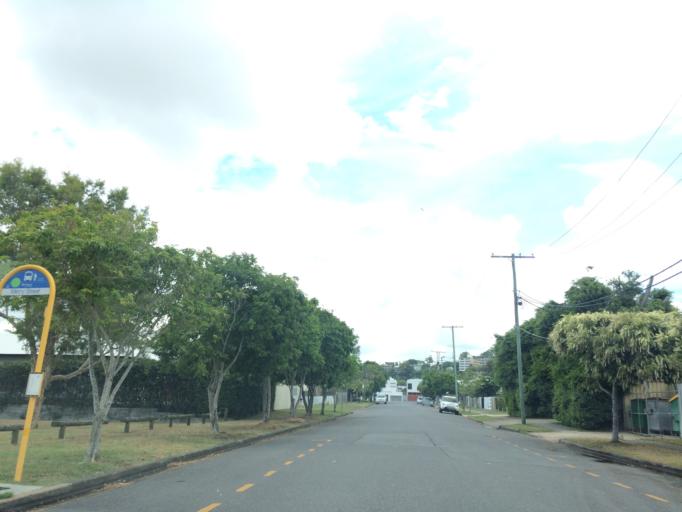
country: AU
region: Queensland
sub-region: Brisbane
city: Ascot
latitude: -27.4446
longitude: 153.0567
